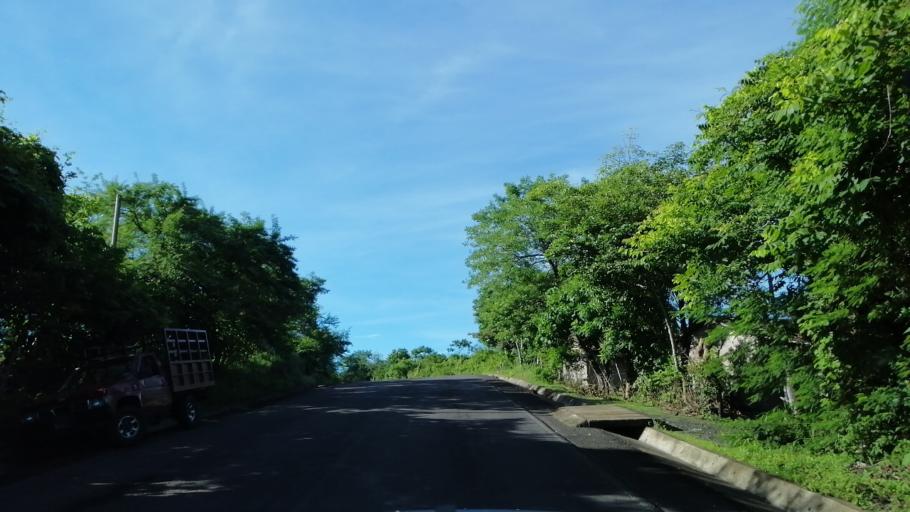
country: SV
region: Morazan
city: Cacaopera
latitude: 13.7850
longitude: -88.1063
